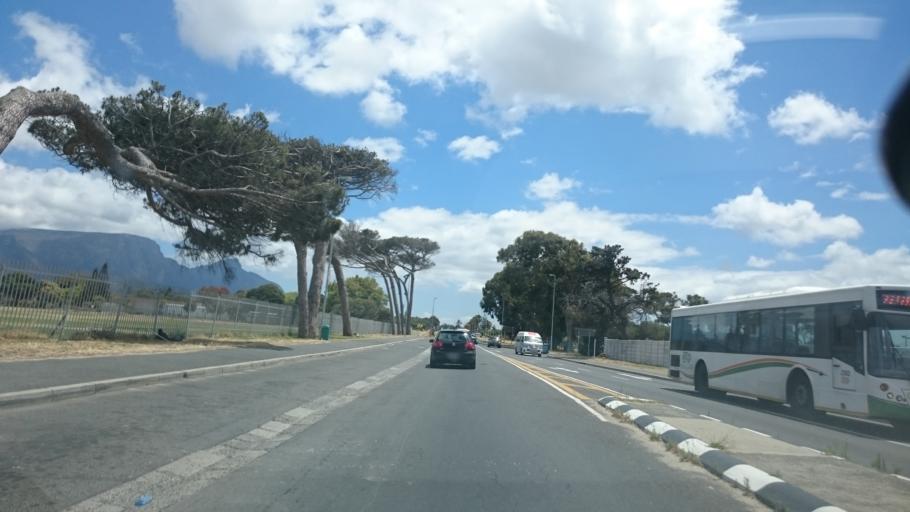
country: ZA
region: Western Cape
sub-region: City of Cape Town
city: Bergvliet
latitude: -34.0599
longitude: 18.4601
